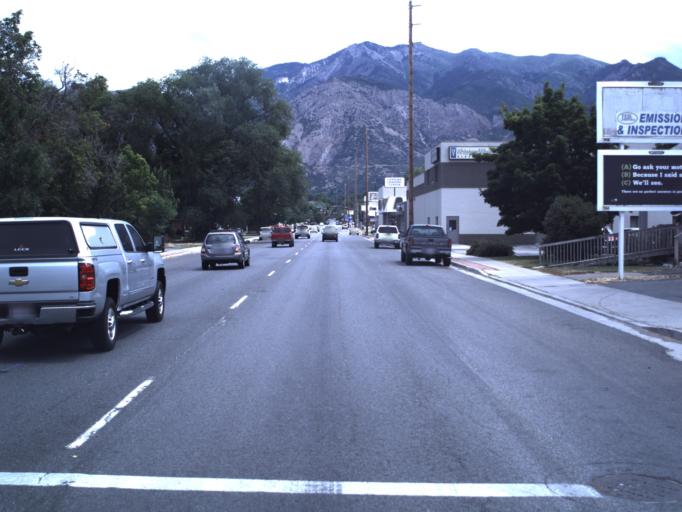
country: US
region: Utah
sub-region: Weber County
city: Ogden
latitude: 41.2082
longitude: -111.9763
